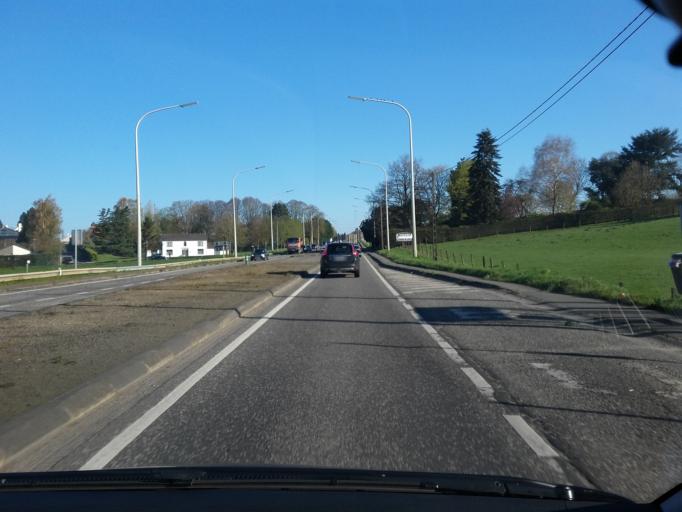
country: BE
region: Wallonia
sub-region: Province du Brabant Wallon
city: Genappe
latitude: 50.6267
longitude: 4.4339
